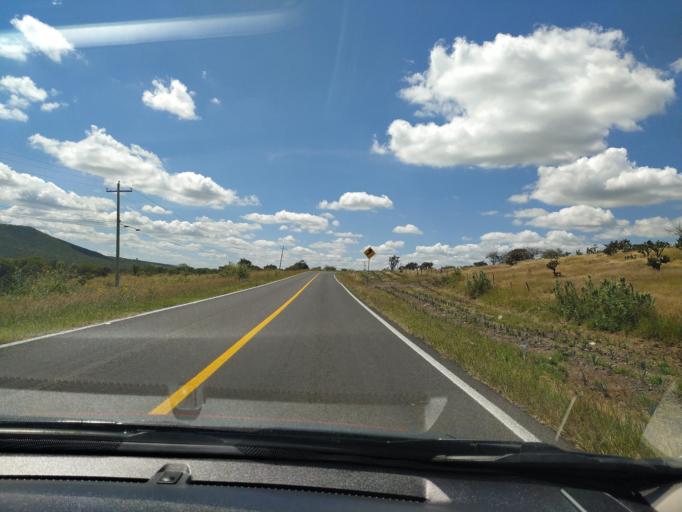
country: MX
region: Jalisco
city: San Miguel el Alto
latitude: 21.0243
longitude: -102.4328
